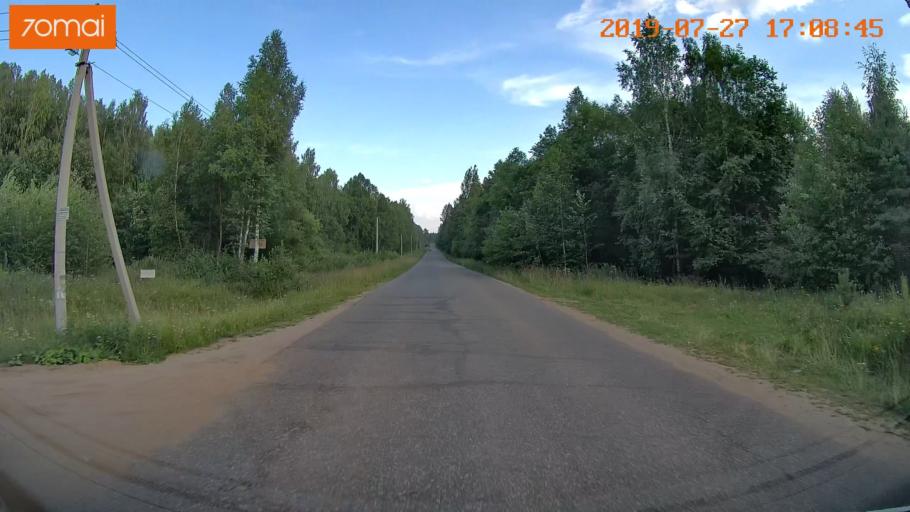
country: RU
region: Ivanovo
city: Novo-Talitsy
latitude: 57.0801
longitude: 40.8410
